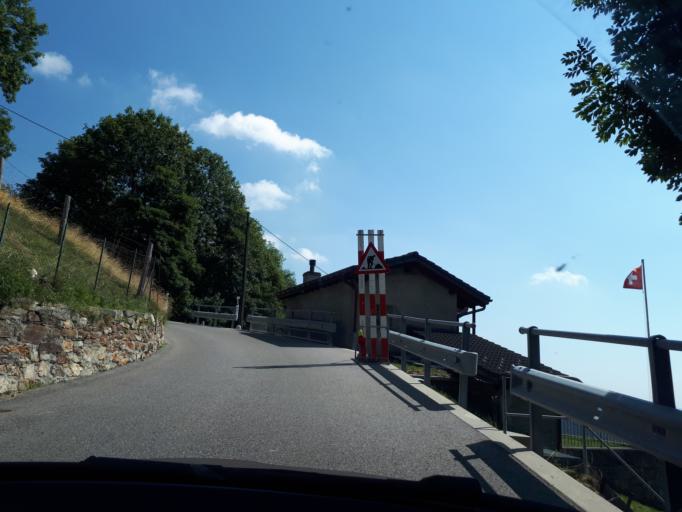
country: CH
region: Ticino
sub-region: Locarno District
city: Magadino
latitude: 46.1027
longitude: 8.8416
